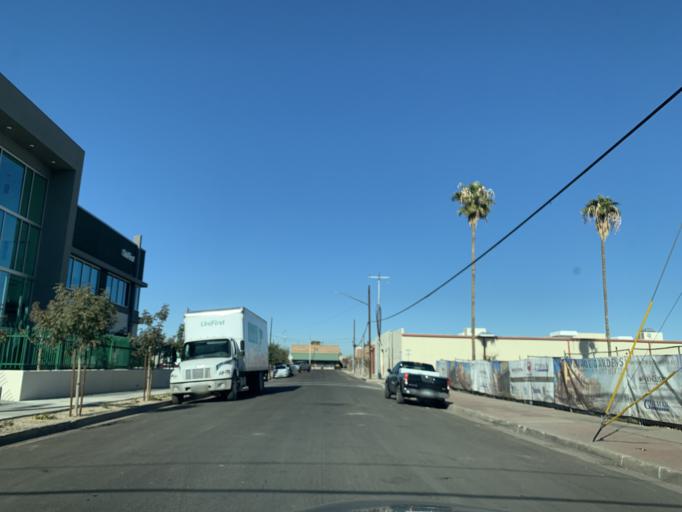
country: US
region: Arizona
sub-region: Maricopa County
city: Phoenix
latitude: 33.4499
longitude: -112.0520
